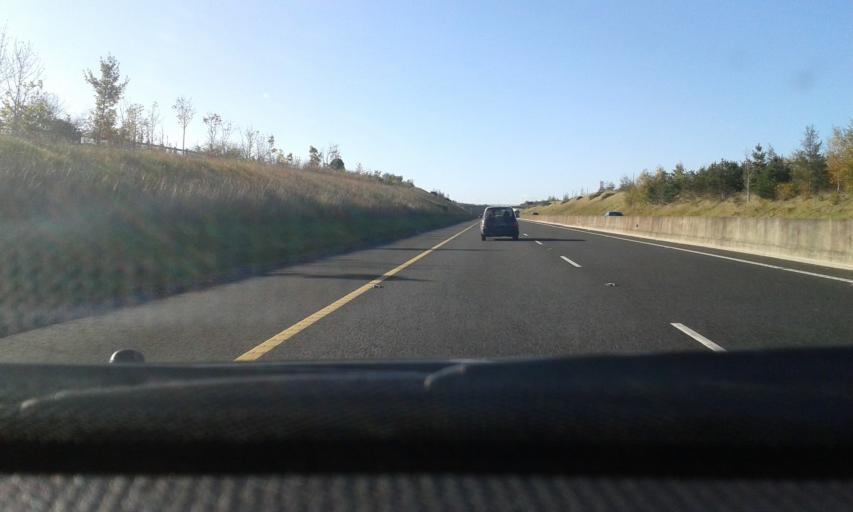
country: IE
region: Leinster
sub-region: Laois
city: Rathdowney
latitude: 52.7170
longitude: -7.6050
